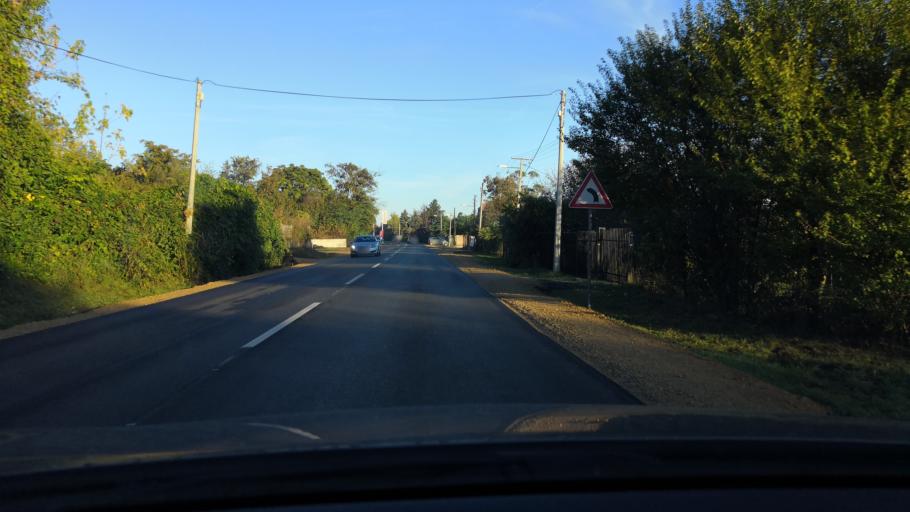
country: RS
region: Autonomna Pokrajina Vojvodina
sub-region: Juznobacki Okrug
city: Petrovaradin
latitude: 45.2303
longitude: 19.8945
